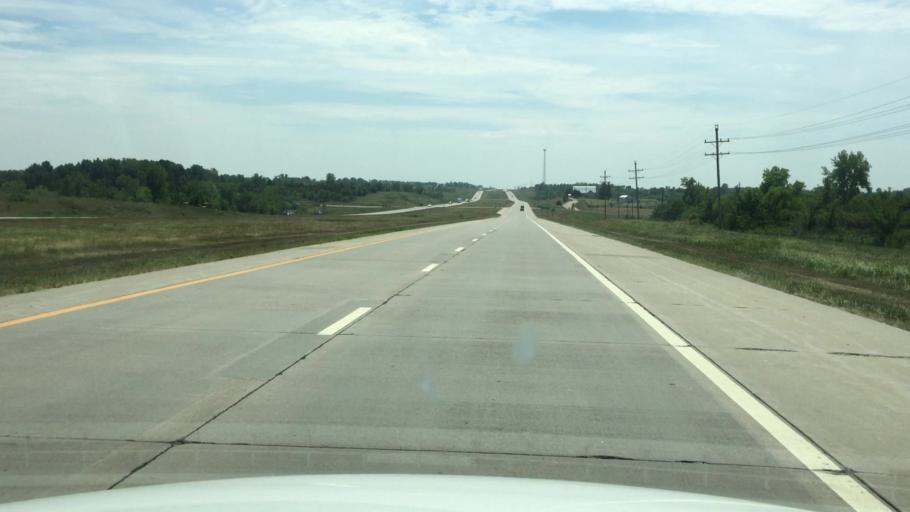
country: US
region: Kansas
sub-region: Jackson County
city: Holton
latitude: 39.2647
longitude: -95.7201
